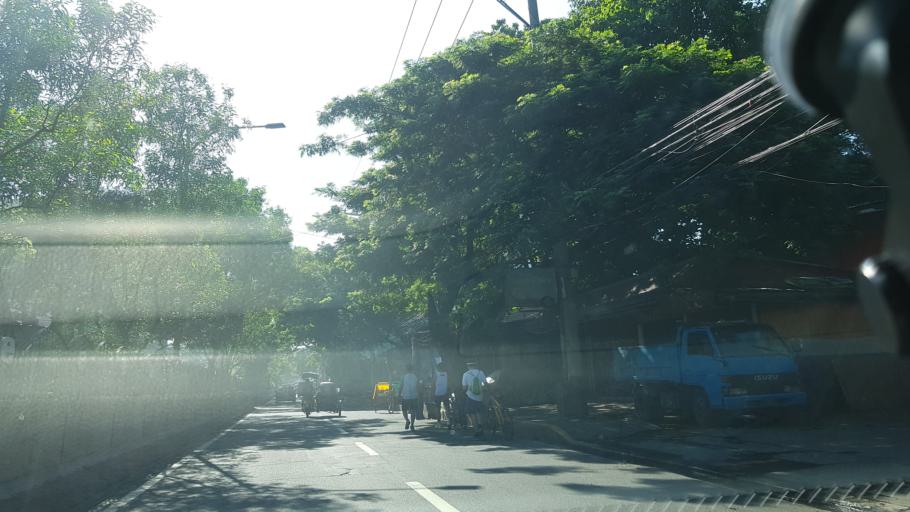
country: PH
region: Metro Manila
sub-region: Pasig
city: Pasig City
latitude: 14.5695
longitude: 121.0835
